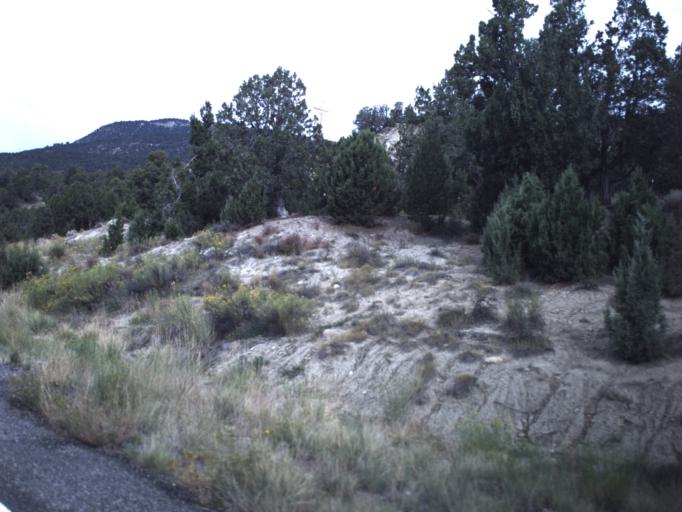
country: US
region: Utah
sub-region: Washington County
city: Hildale
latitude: 37.2620
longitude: -112.7847
